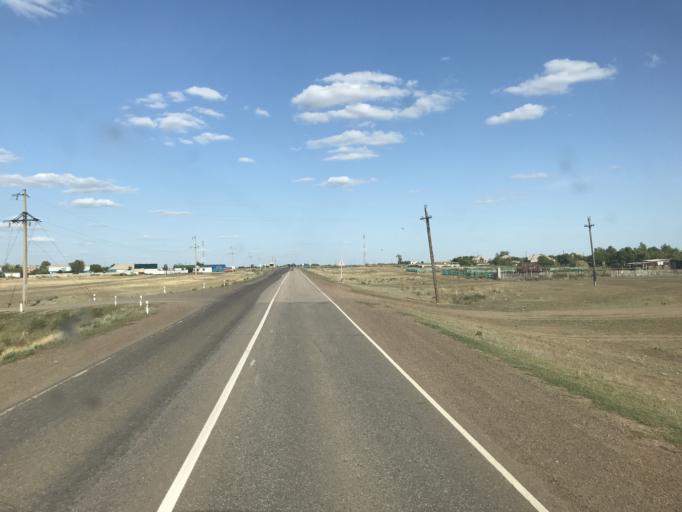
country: KZ
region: Aqmola
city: Esil
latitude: 51.8967
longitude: 66.7532
